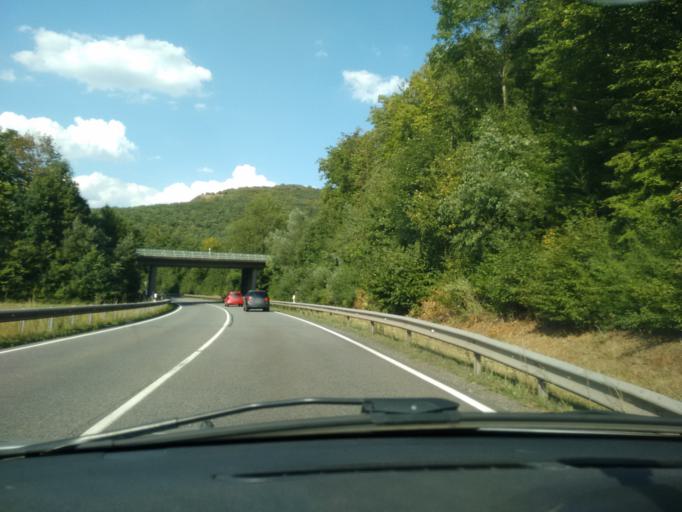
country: DE
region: Rheinland-Pfalz
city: Meckenbach
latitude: 49.7867
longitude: 7.4876
